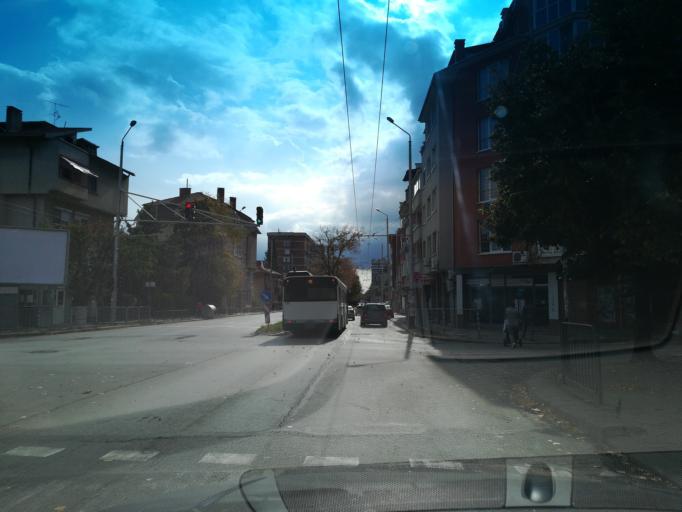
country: BG
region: Stara Zagora
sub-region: Obshtina Stara Zagora
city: Stara Zagora
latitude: 42.4333
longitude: 25.6321
